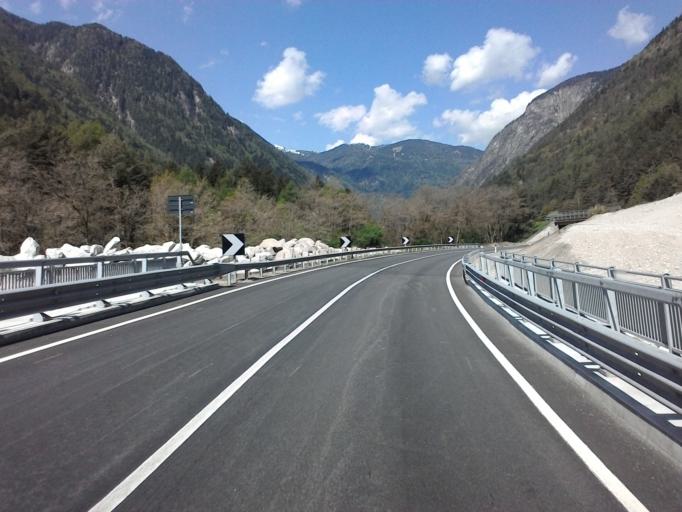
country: IT
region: Trentino-Alto Adige
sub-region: Bolzano
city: Fortezza
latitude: 46.8035
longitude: 11.5876
